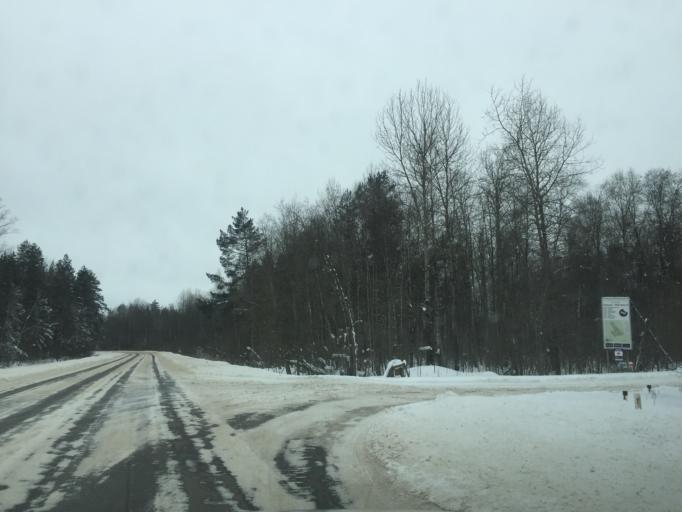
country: RU
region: Leningrad
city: Imeni Sverdlova
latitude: 59.8510
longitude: 30.6616
